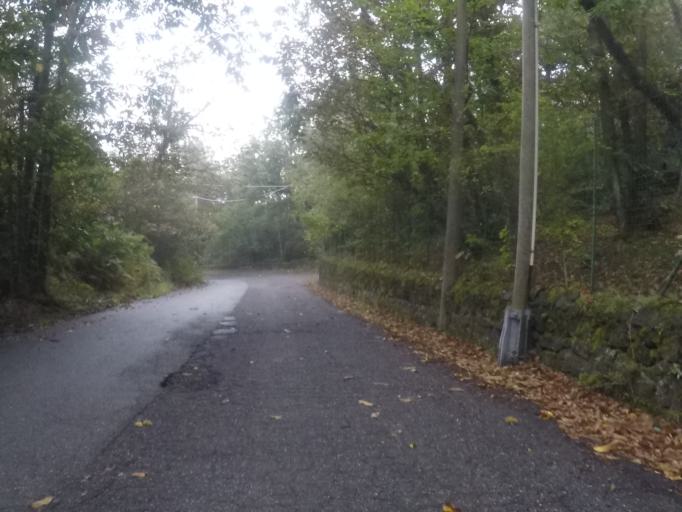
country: IT
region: Sicily
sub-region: Catania
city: Pedara
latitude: 37.6573
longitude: 15.0413
